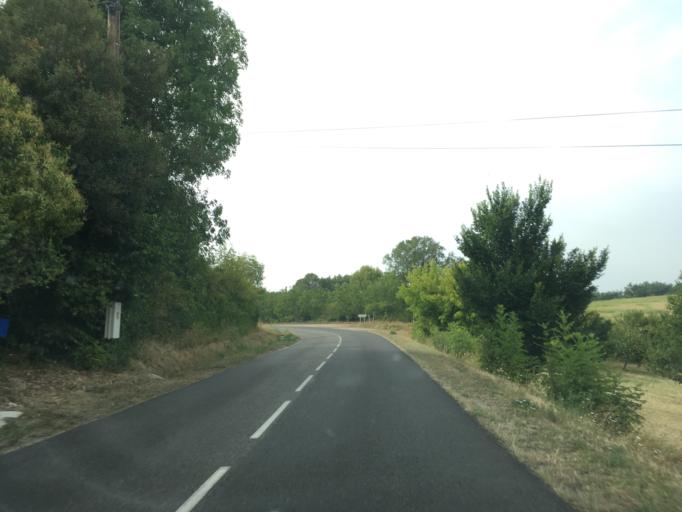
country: FR
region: Midi-Pyrenees
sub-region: Departement du Lot
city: Souillac
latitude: 44.8438
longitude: 1.5484
